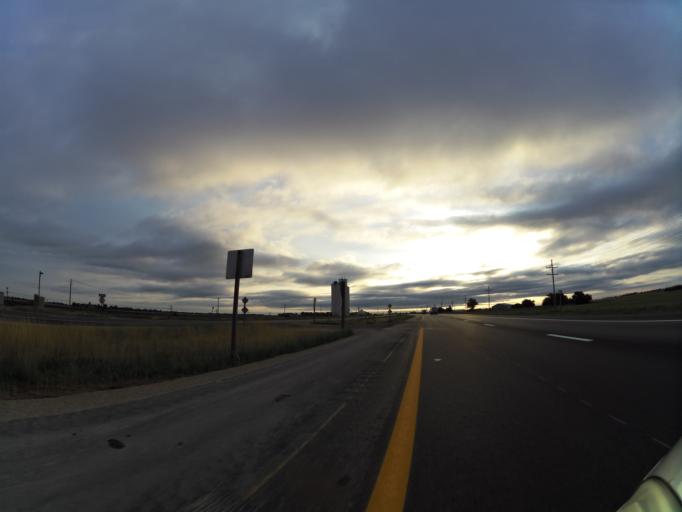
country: US
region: Kansas
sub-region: Reno County
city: South Hutchinson
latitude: 38.0046
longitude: -98.0184
